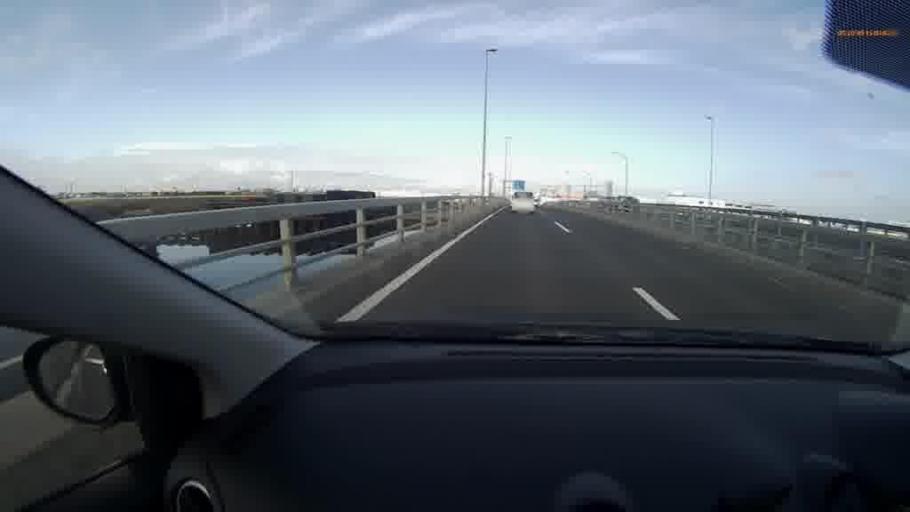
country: JP
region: Hokkaido
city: Kushiro
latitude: 43.0036
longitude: 144.4182
